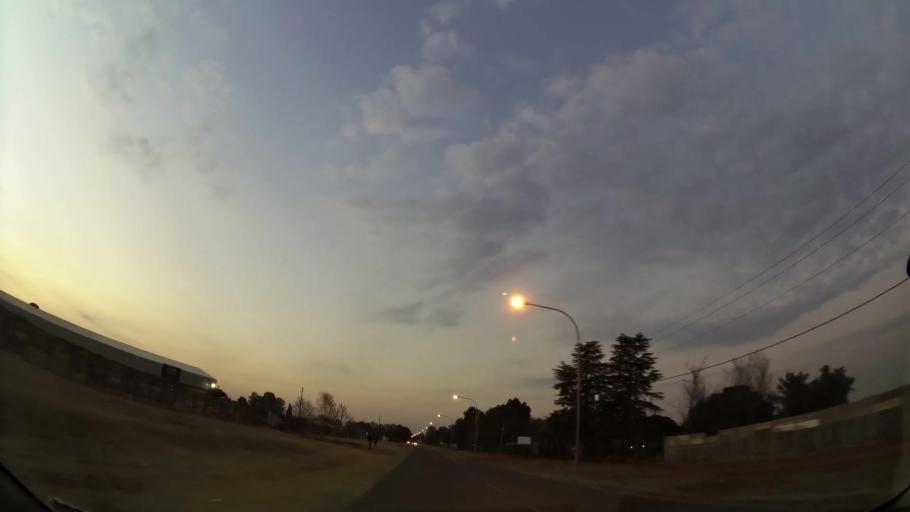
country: ZA
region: Gauteng
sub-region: Ekurhuleni Metropolitan Municipality
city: Benoni
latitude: -26.1375
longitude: 28.3142
